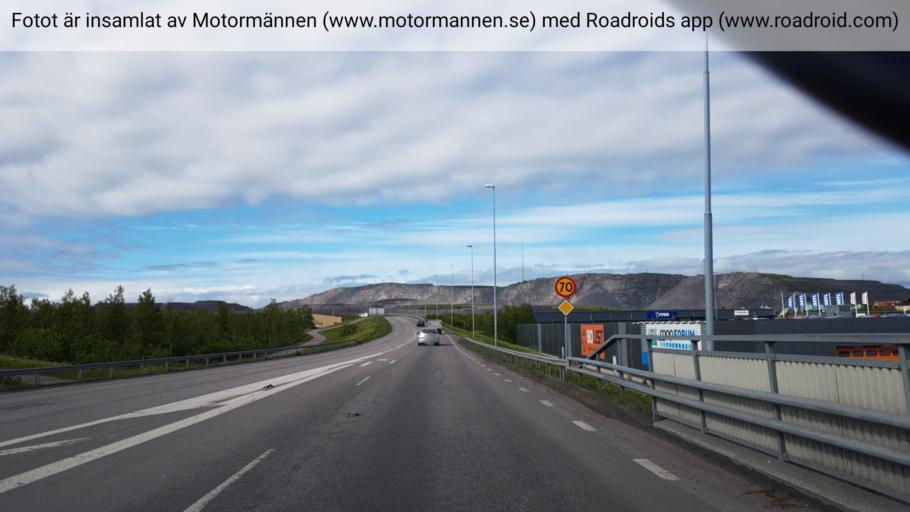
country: SE
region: Norrbotten
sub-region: Kiruna Kommun
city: Kiruna
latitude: 67.8438
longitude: 20.2579
